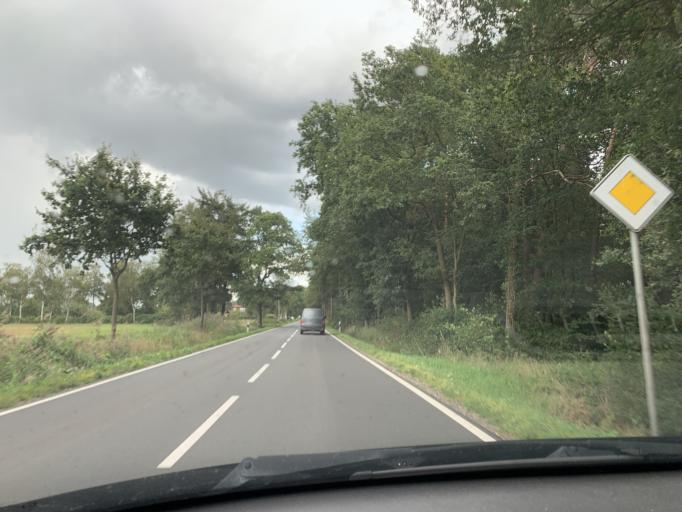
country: DE
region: Lower Saxony
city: Westerstede
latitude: 53.2853
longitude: 7.9932
